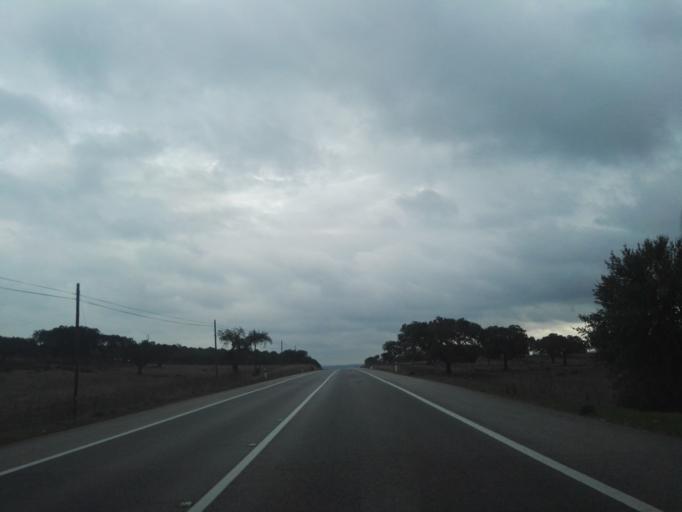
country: PT
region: Portalegre
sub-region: Arronches
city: Arronches
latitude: 39.1508
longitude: -7.3107
